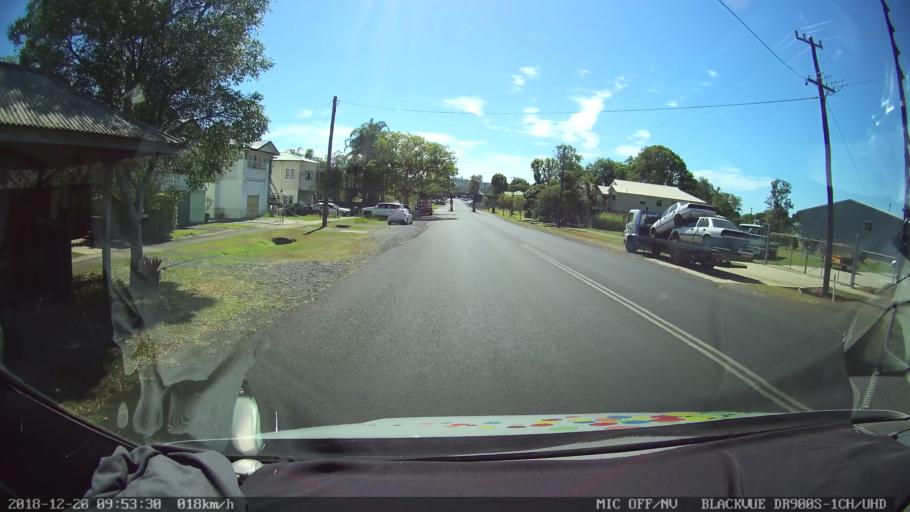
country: AU
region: New South Wales
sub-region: Lismore Municipality
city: Lismore
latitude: -28.8015
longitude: 153.2698
